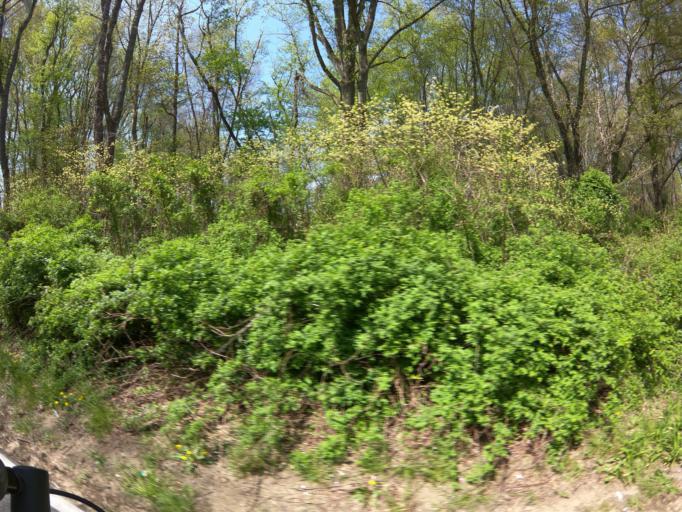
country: US
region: Delaware
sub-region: New Castle County
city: Delaware City
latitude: 39.5368
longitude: -75.6707
